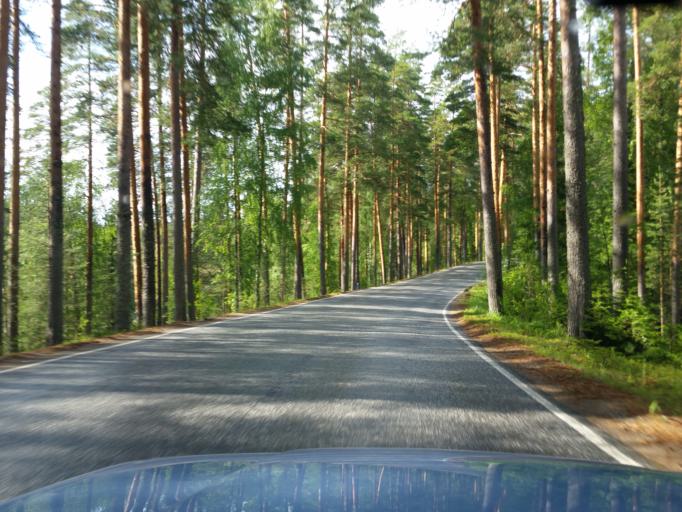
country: FI
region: Southern Savonia
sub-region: Savonlinna
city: Sulkava
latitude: 61.7936
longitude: 28.4189
